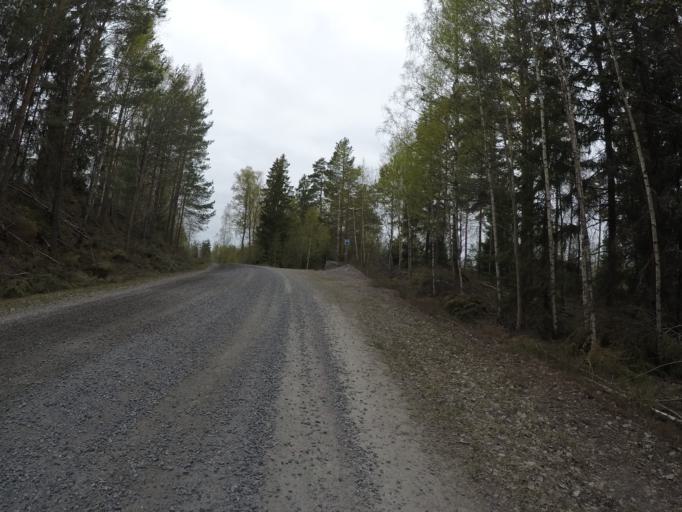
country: SE
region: Soedermanland
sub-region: Eskilstuna Kommun
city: Kvicksund
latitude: 59.3898
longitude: 16.3174
